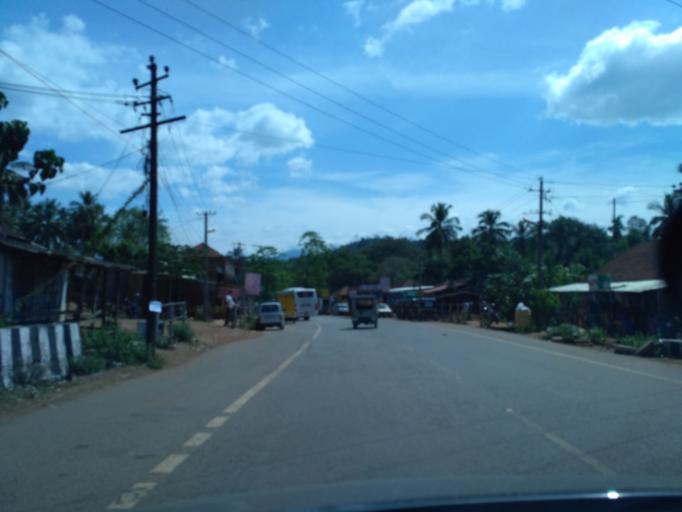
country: IN
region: Karnataka
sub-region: Dakshina Kannada
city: Sulya
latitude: 12.5026
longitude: 75.5343
